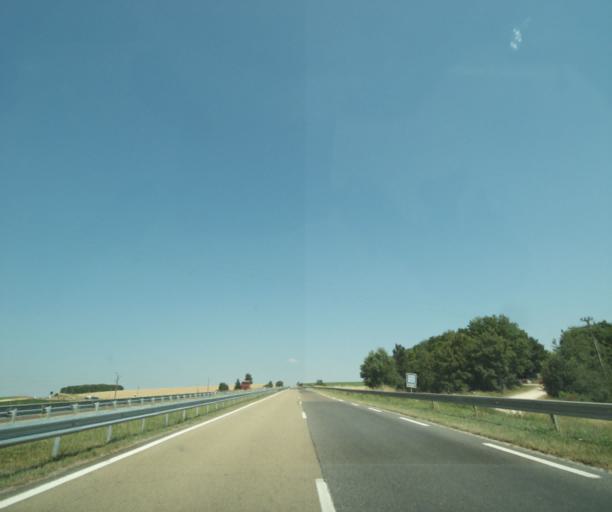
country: FR
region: Champagne-Ardenne
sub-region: Departement de la Marne
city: Fagnieres
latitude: 49.0453
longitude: 4.3073
